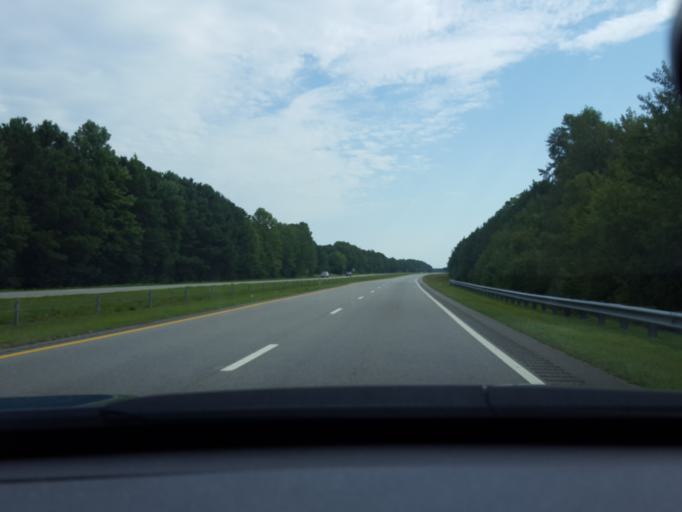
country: US
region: North Carolina
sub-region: Chowan County
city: Edenton
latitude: 36.0673
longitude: -76.6421
